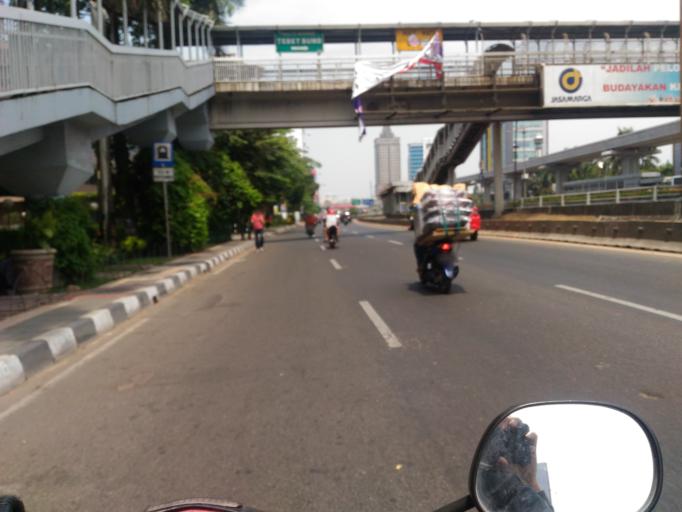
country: ID
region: Jakarta Raya
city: Jakarta
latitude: -6.2430
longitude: 106.8513
